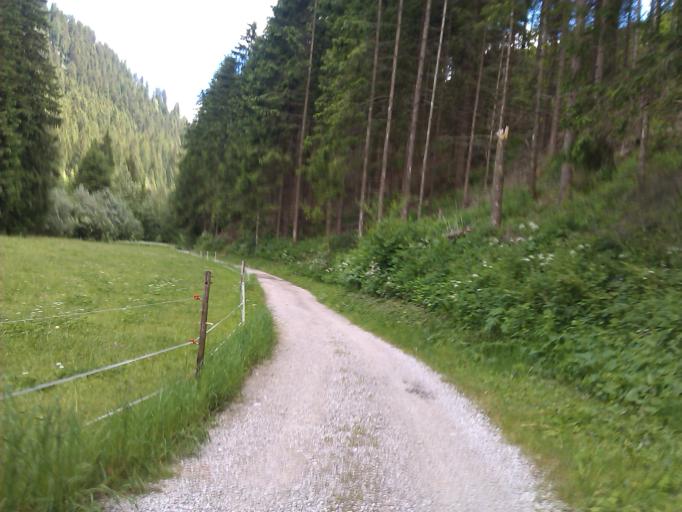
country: AT
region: Tyrol
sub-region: Politischer Bezirk Reutte
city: Lermoos
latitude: 47.4127
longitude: 10.8555
